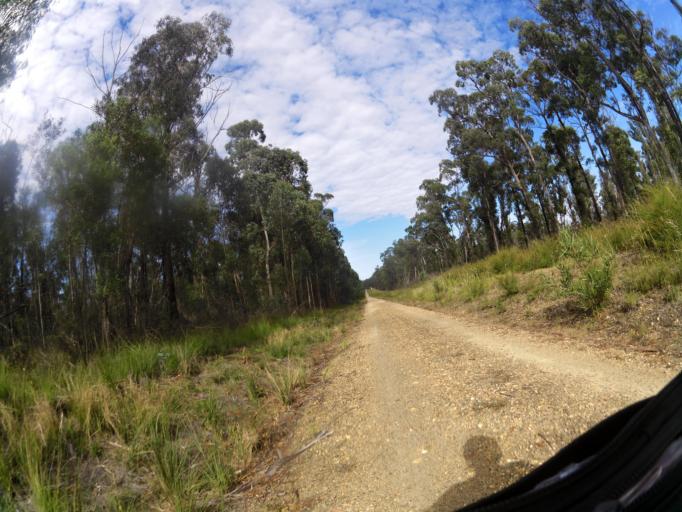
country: AU
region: Victoria
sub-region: East Gippsland
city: Lakes Entrance
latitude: -37.7467
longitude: 148.2332
